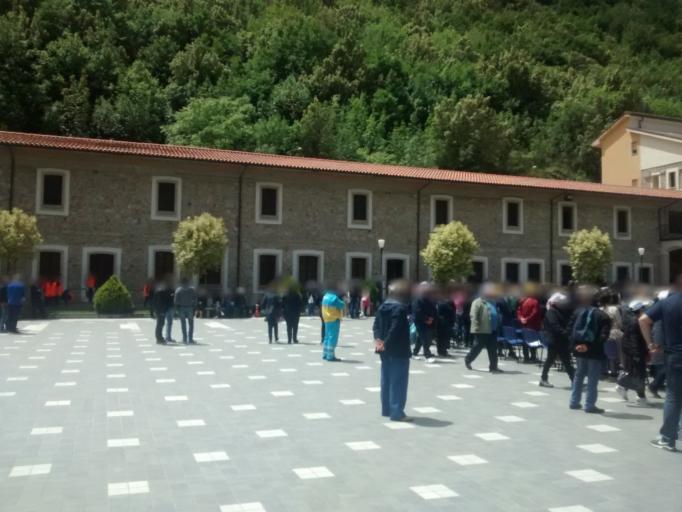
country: IT
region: Calabria
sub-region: Provincia di Cosenza
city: San Sosti
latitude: 39.6663
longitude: 16.0037
